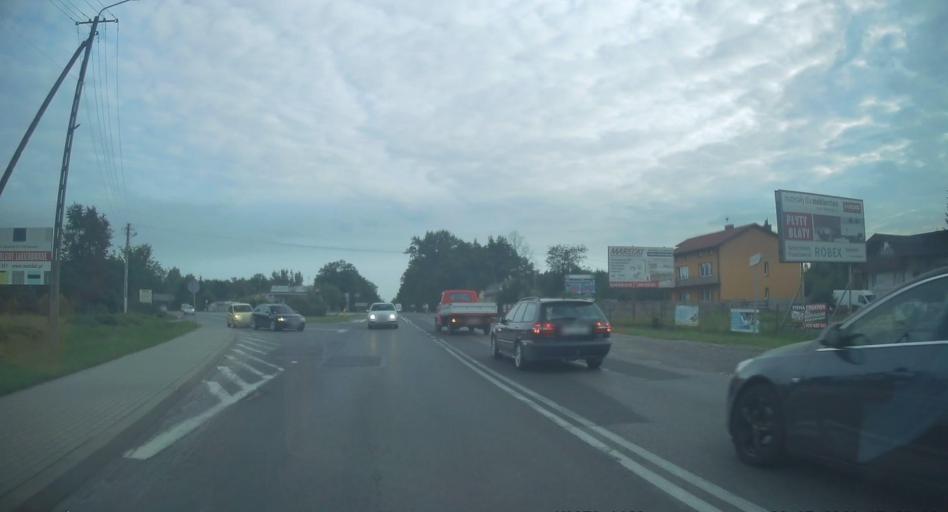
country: PL
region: Lodz Voivodeship
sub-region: Powiat radomszczanski
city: Radomsko
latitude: 51.0437
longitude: 19.4379
